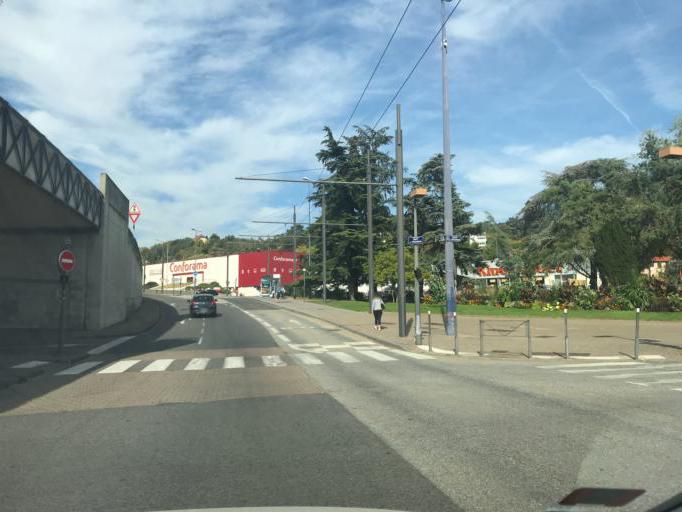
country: FR
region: Rhone-Alpes
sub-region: Departement du Rhone
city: Caluire-et-Cuire
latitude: 45.7912
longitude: 4.8608
